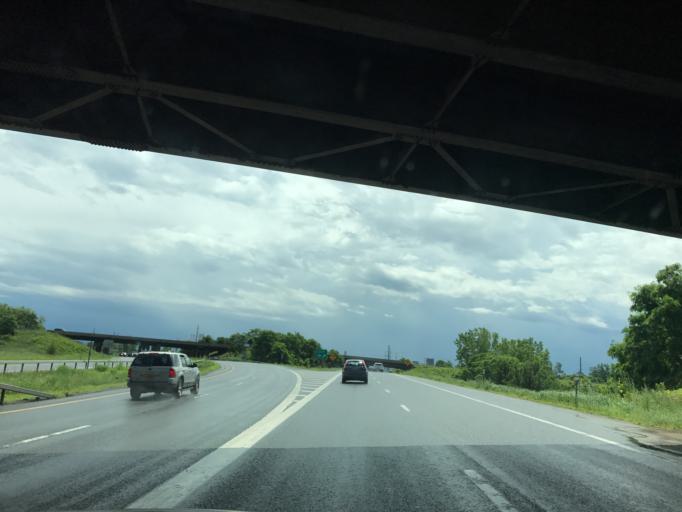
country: US
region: New York
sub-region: Albany County
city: McKownville
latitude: 42.6957
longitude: -73.8414
